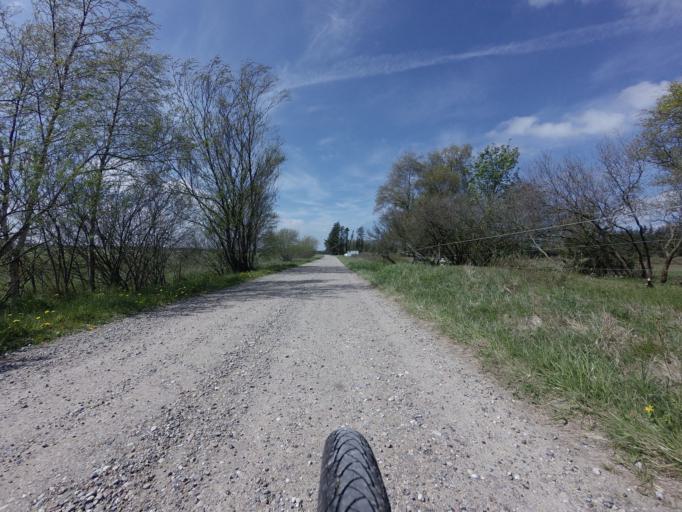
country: DK
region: North Denmark
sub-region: Jammerbugt Kommune
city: Brovst
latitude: 57.1549
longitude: 9.5741
